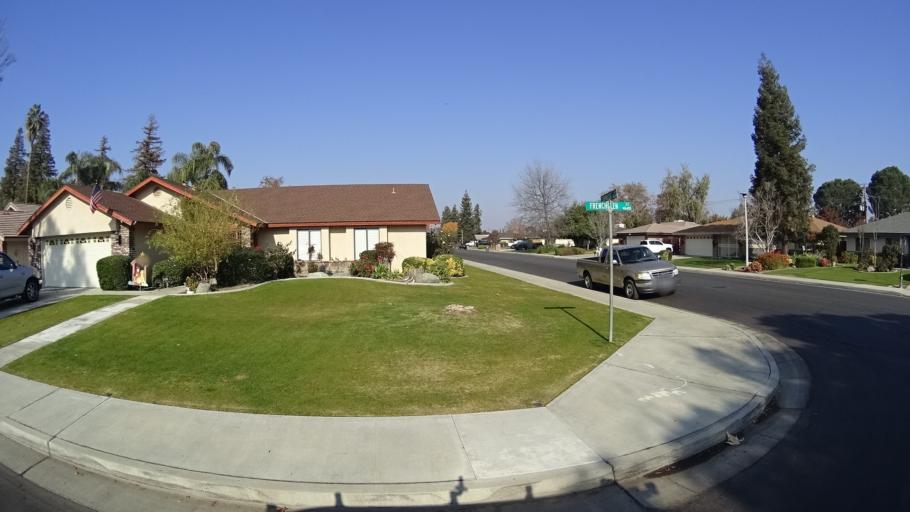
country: US
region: California
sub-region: Kern County
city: Greenacres
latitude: 35.3256
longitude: -119.0756
